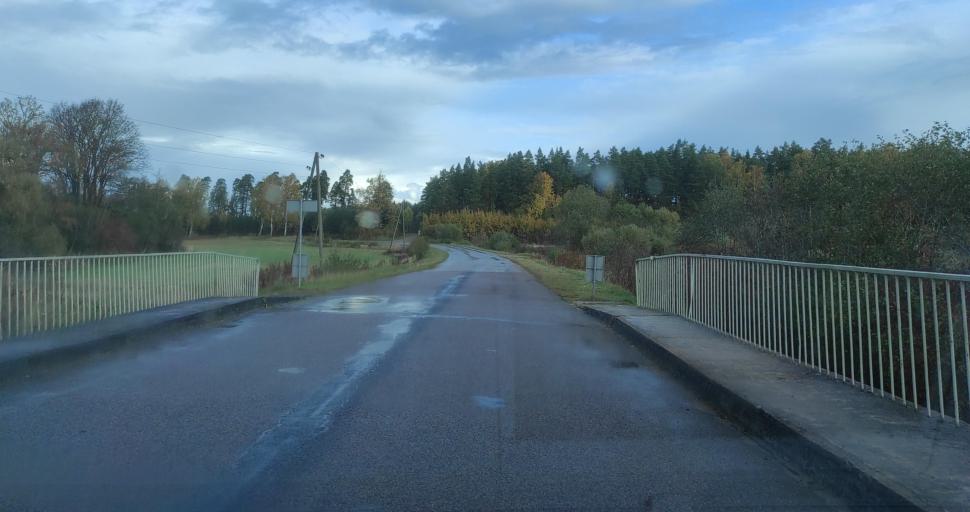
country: LV
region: Skrunda
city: Skrunda
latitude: 56.6803
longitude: 22.0701
